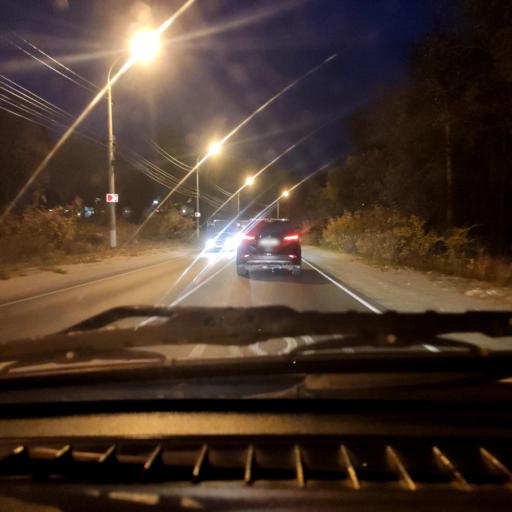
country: RU
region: Samara
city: Tol'yatti
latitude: 53.4861
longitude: 49.3127
